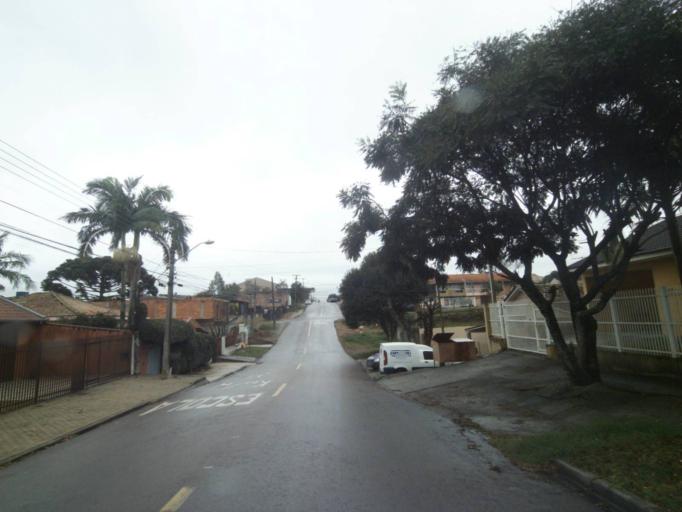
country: BR
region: Parana
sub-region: Curitiba
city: Curitiba
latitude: -25.5143
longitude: -49.3008
